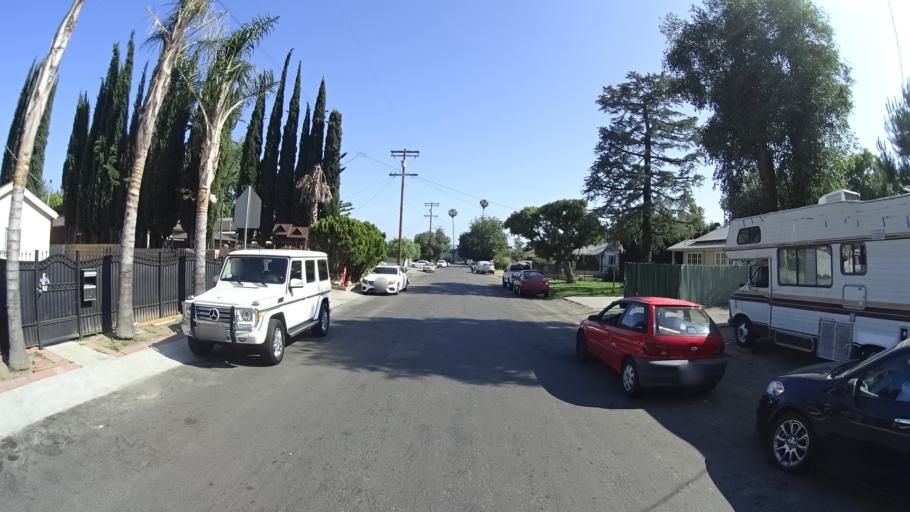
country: US
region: California
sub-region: Los Angeles County
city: Van Nuys
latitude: 34.1901
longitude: -118.4302
